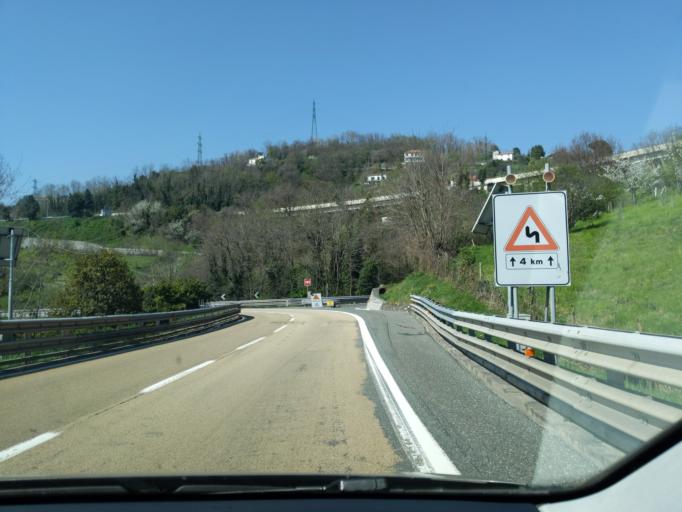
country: IT
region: Liguria
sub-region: Provincia di Genova
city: Pedemonte
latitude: 44.5043
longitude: 8.9224
